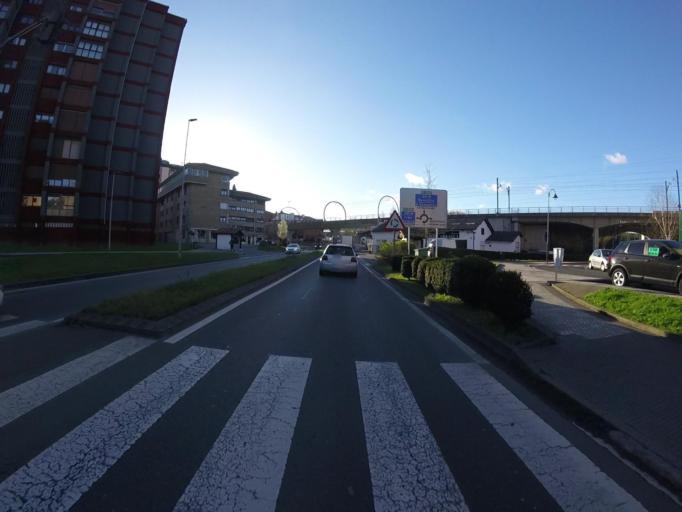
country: ES
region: Basque Country
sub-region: Provincia de Guipuzcoa
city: Lezo
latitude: 43.3090
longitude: -1.8824
